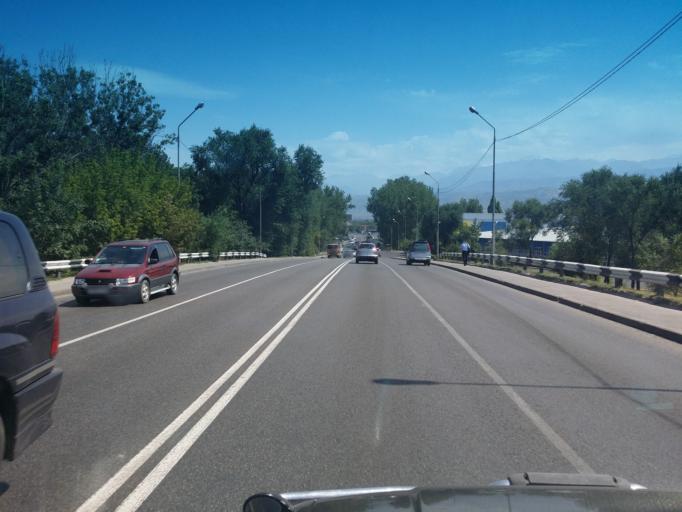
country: KZ
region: Almaty Oblysy
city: Pervomayskiy
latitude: 43.3423
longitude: 76.9784
